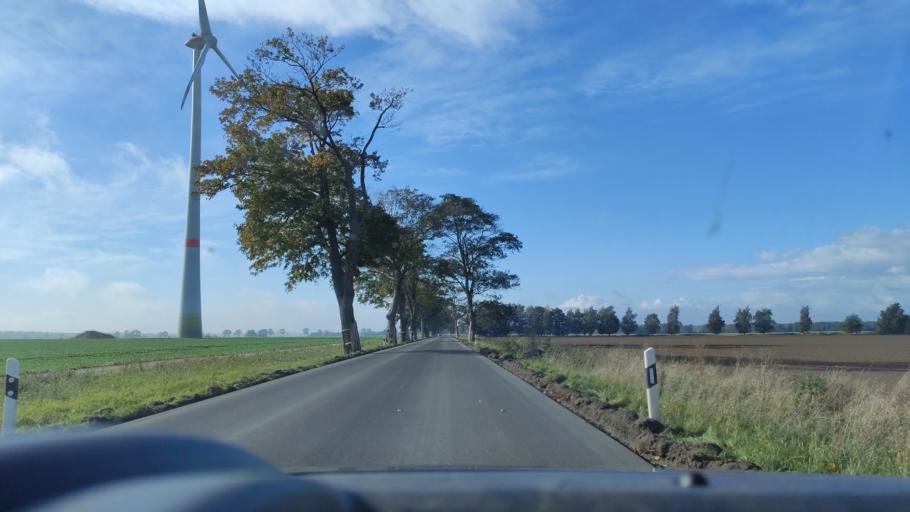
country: DE
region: Mecklenburg-Vorpommern
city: Grimmen
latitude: 54.0565
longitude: 13.1419
